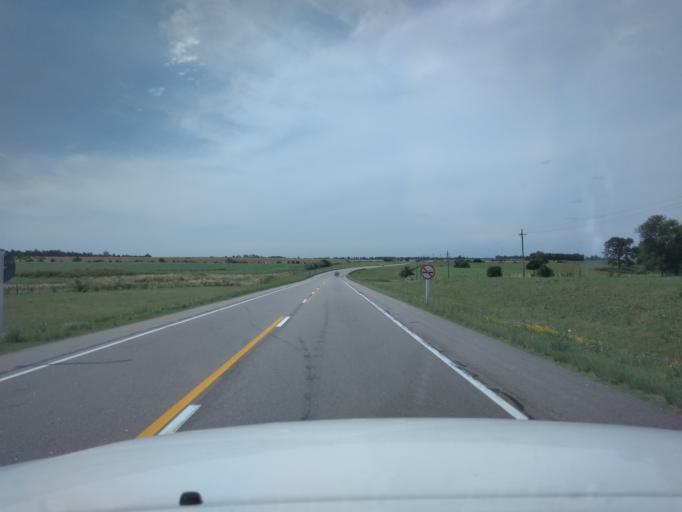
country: UY
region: Florida
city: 25 de Mayo
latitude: -34.2343
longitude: -56.2131
